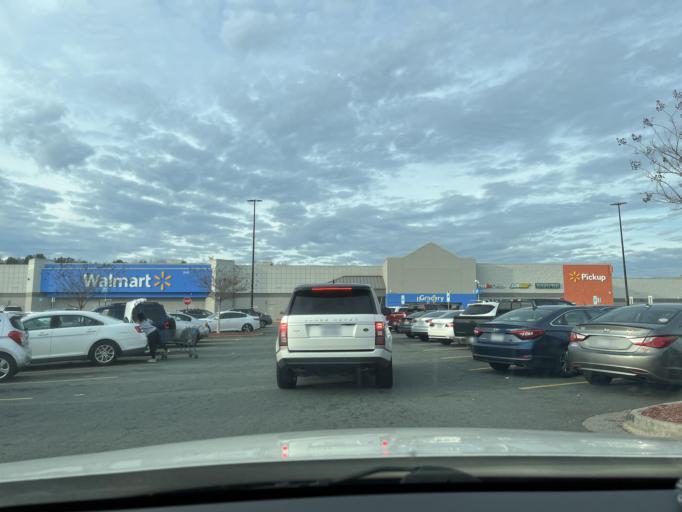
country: US
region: North Carolina
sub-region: Alamance County
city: Elon
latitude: 36.0711
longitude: -79.4982
